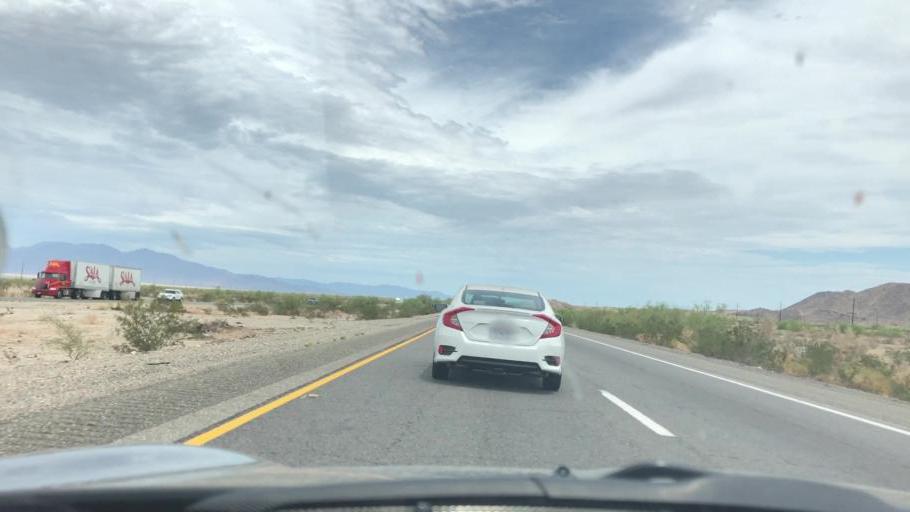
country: US
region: California
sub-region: Imperial County
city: Niland
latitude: 33.7091
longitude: -115.3689
